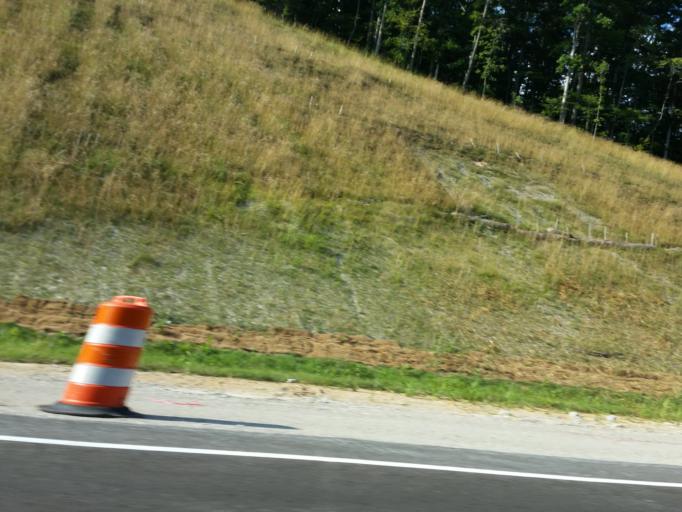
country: US
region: Tennessee
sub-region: Maury County
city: Mount Pleasant
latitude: 35.5649
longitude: -87.3549
